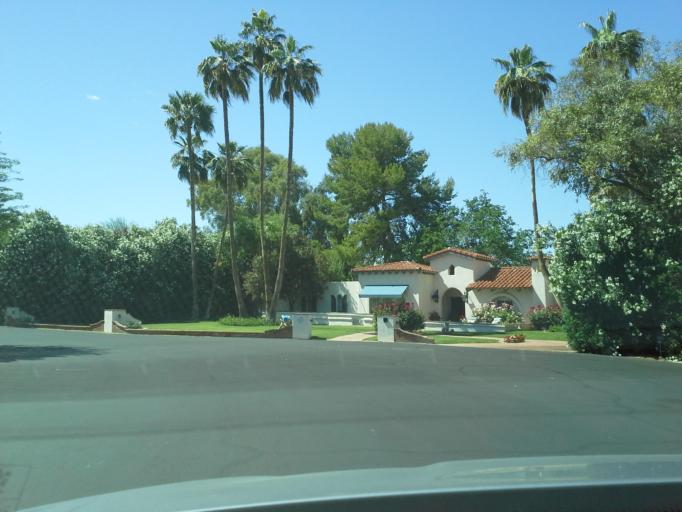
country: US
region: Arizona
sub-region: Maricopa County
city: Paradise Valley
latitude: 33.5583
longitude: -111.9276
